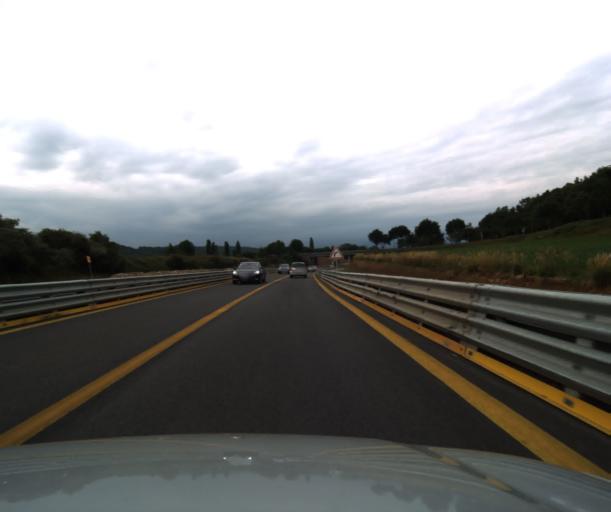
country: FR
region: Midi-Pyrenees
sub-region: Departement des Hautes-Pyrenees
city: Juillan
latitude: 43.1852
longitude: 0.0112
